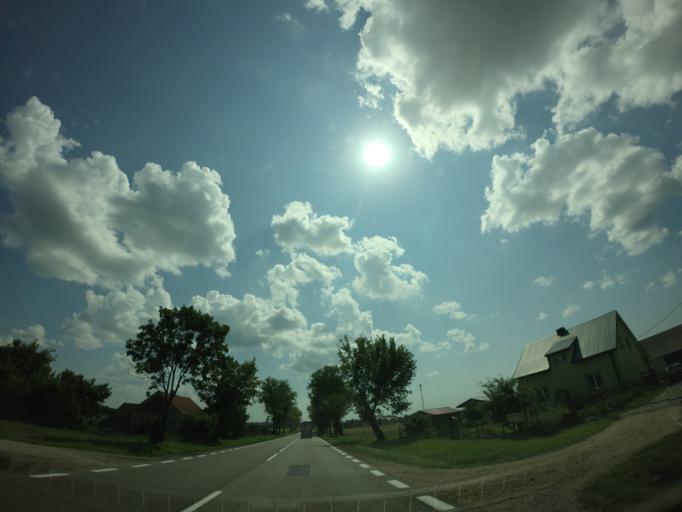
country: PL
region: Podlasie
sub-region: Powiat lomzynski
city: Piatnica
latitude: 53.2617
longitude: 22.1258
